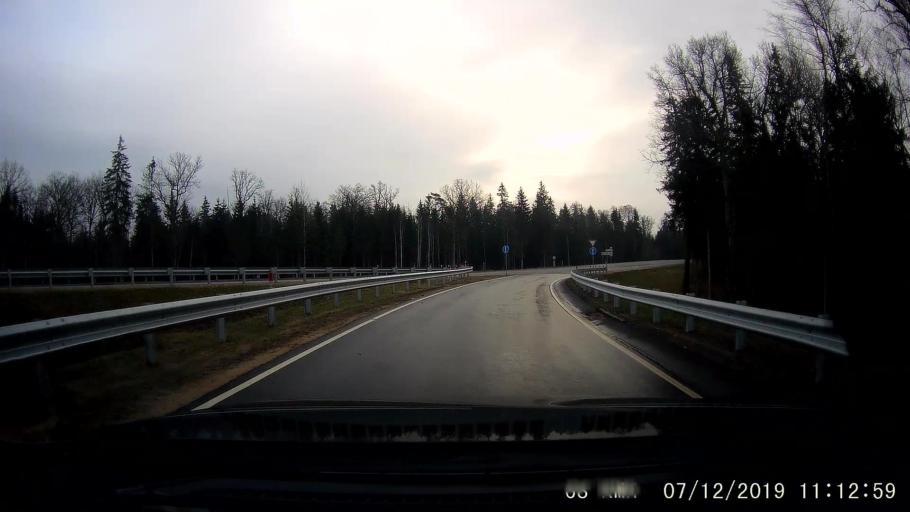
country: BY
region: Grodnenskaya
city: Iwye
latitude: 53.8800
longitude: 25.7391
